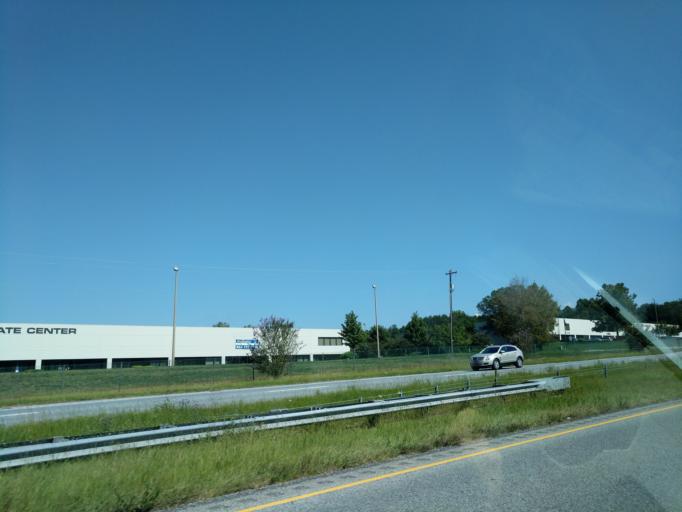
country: US
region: South Carolina
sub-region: Spartanburg County
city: Valley Falls
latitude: 34.9982
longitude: -81.9365
